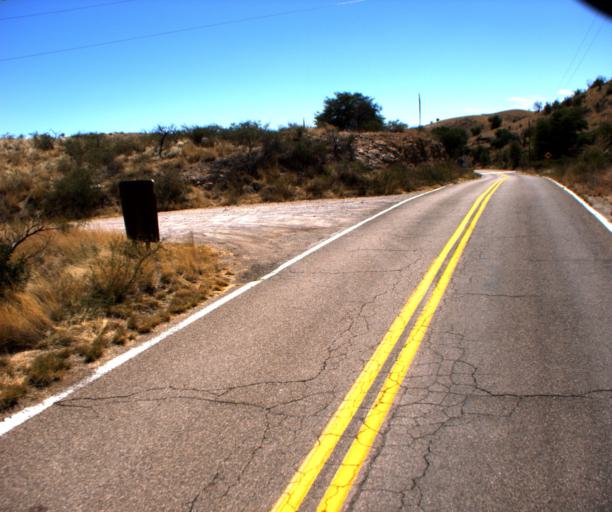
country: US
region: Arizona
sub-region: Santa Cruz County
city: Rio Rico
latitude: 31.3954
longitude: -111.0835
